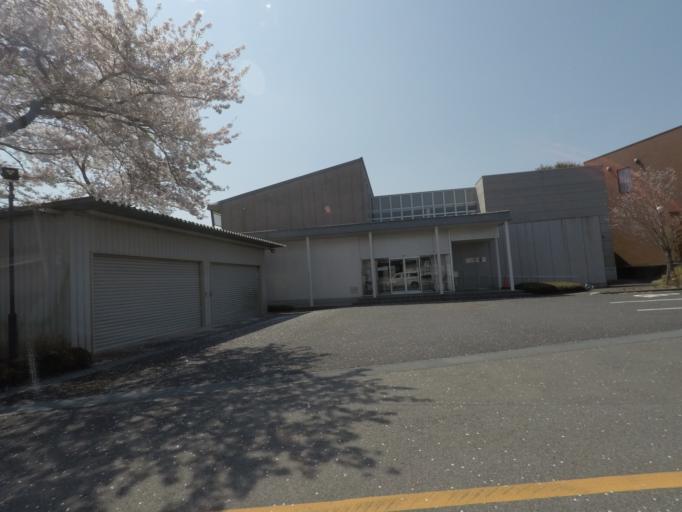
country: JP
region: Chiba
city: Naruto
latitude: 35.6929
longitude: 140.4149
